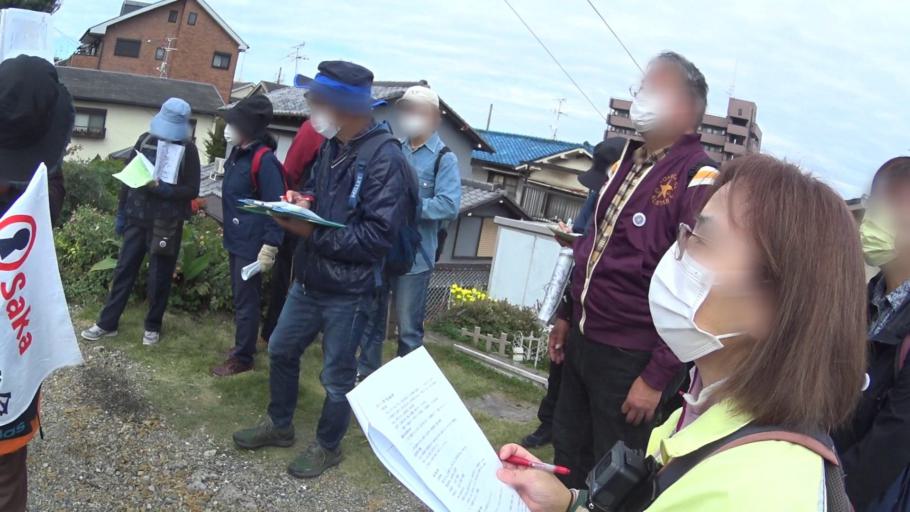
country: JP
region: Osaka
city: Kashihara
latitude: 34.5523
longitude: 135.6045
